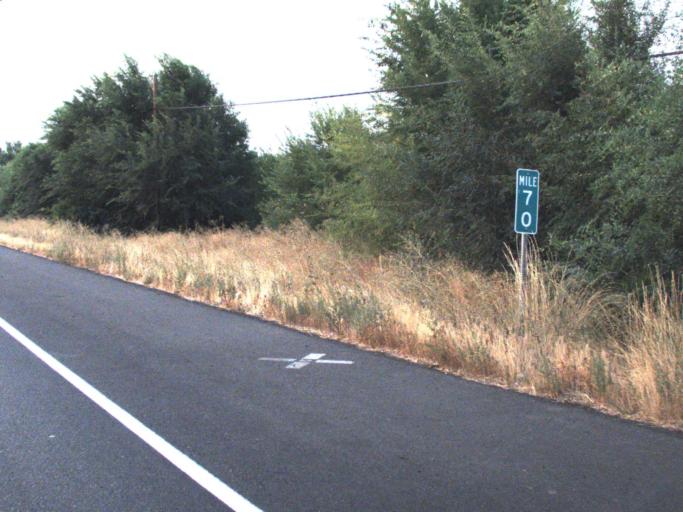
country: US
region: Washington
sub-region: Yakima County
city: Wapato
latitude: 46.4604
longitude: -120.4336
